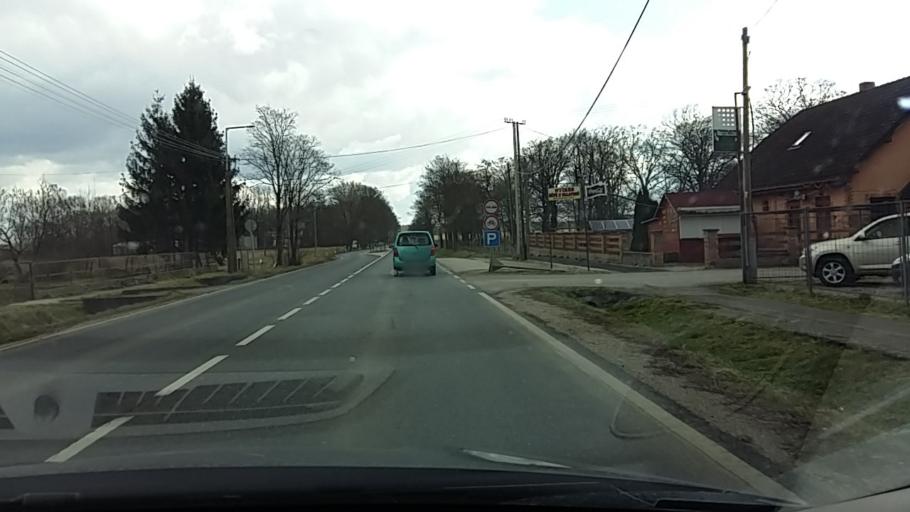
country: HU
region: Somogy
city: Bohonye
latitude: 46.4083
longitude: 17.4090
